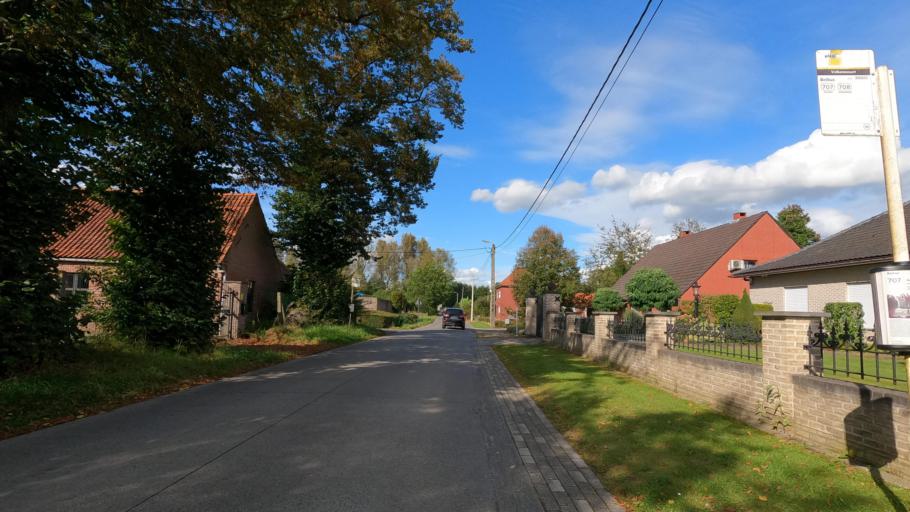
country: BE
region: Flanders
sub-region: Provincie Antwerpen
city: Herselt
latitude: 51.0219
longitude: 4.9158
